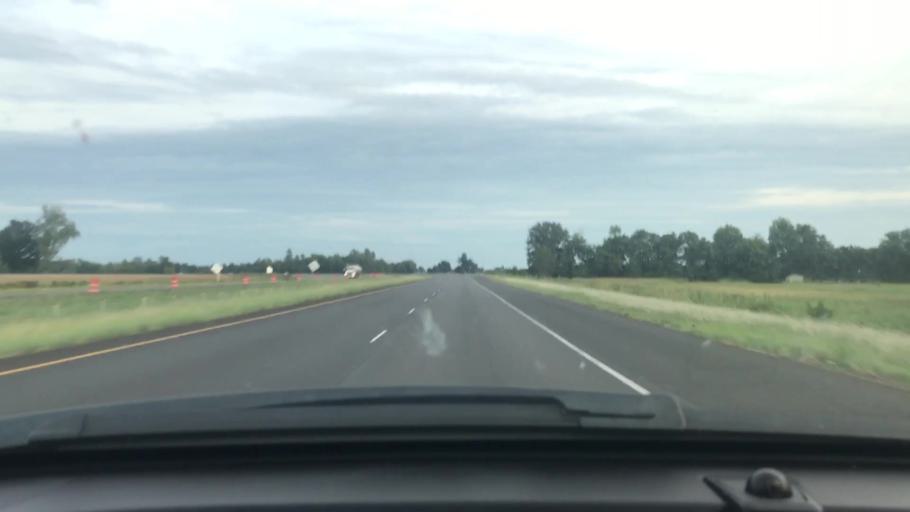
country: US
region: Arkansas
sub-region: Poinsett County
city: Trumann
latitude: 35.6662
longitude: -90.5517
